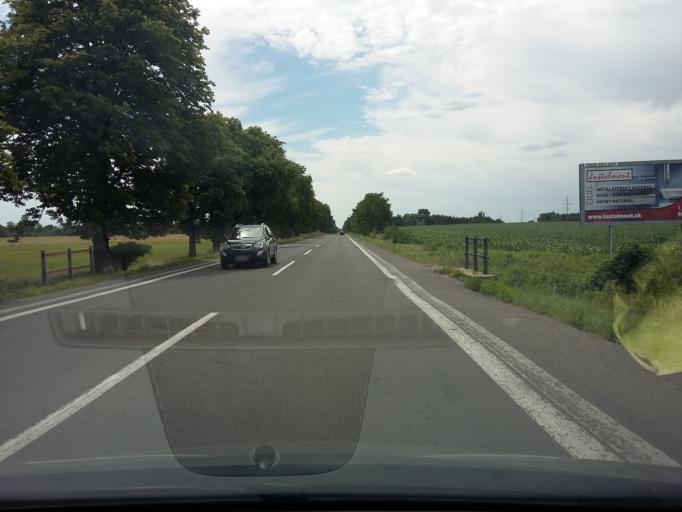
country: SK
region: Bratislavsky
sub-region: Okres Malacky
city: Malacky
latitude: 48.4770
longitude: 17.0129
